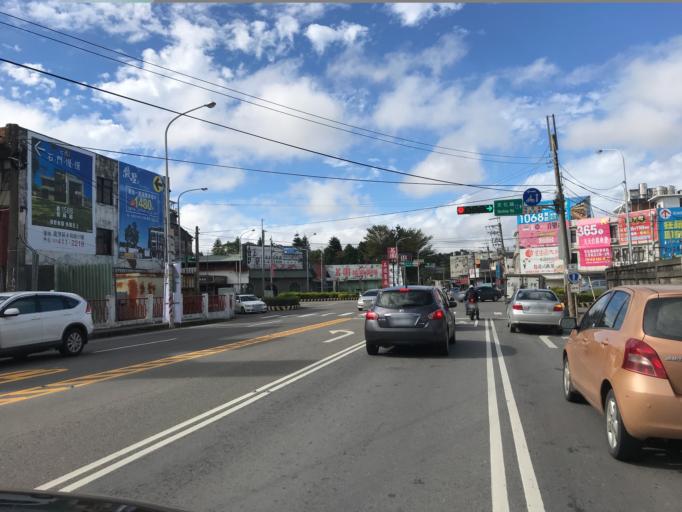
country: TW
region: Taiwan
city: Daxi
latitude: 24.8485
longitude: 121.2453
